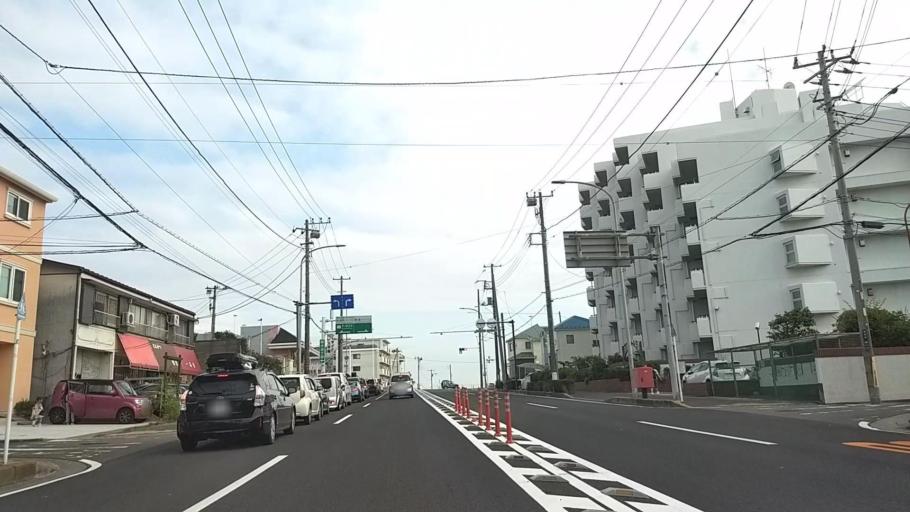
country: JP
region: Kanagawa
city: Hiratsuka
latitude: 35.3179
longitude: 139.3619
